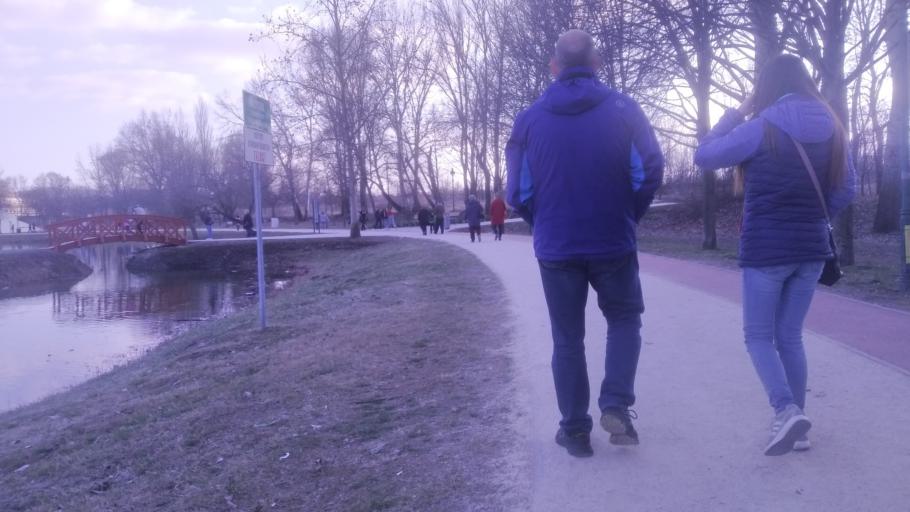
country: HU
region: Komarom-Esztergom
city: Tatabanya
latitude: 47.5765
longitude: 18.3986
